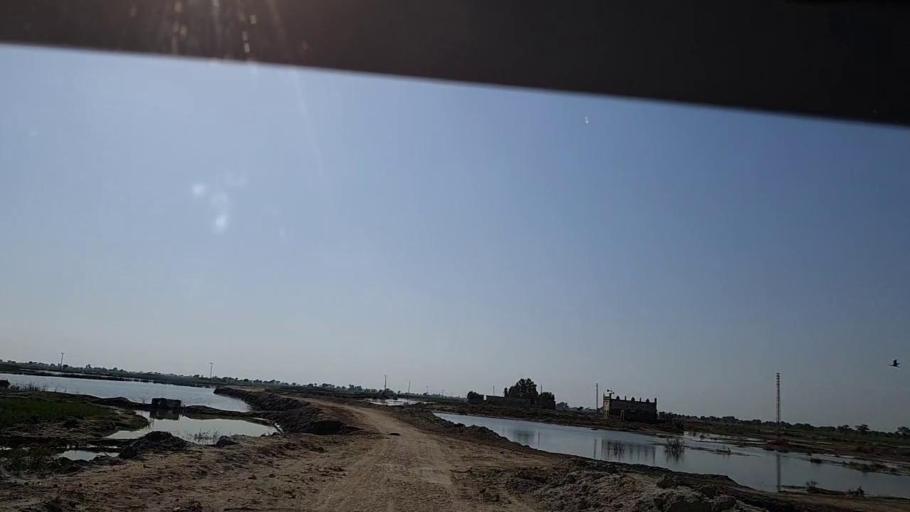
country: PK
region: Sindh
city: Tangwani
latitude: 28.3611
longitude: 69.0290
